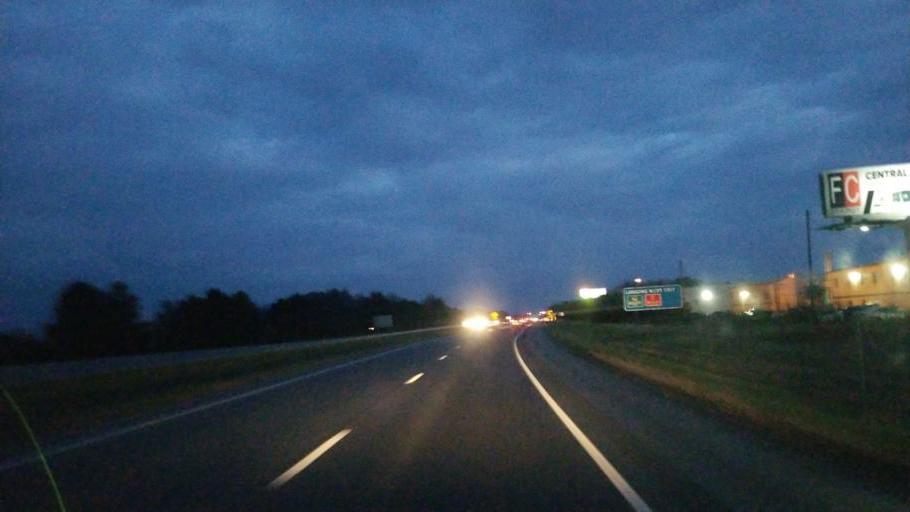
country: US
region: Ohio
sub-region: Wyandot County
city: Upper Sandusky
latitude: 40.8562
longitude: -83.2685
